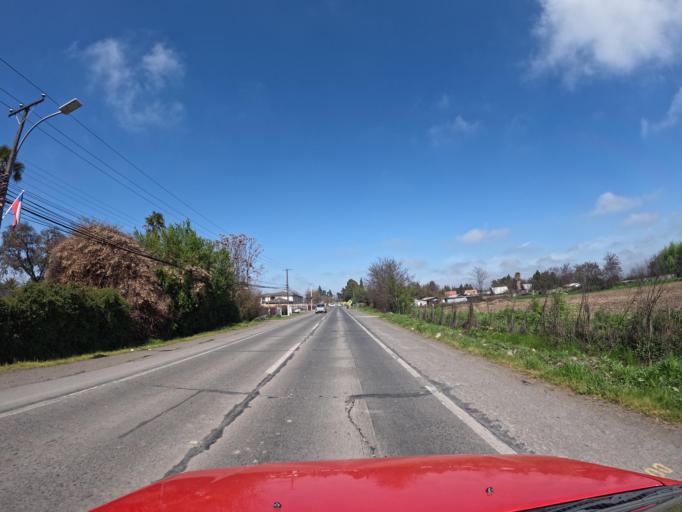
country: CL
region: Maule
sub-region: Provincia de Curico
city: Molina
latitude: -35.0709
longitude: -71.2560
